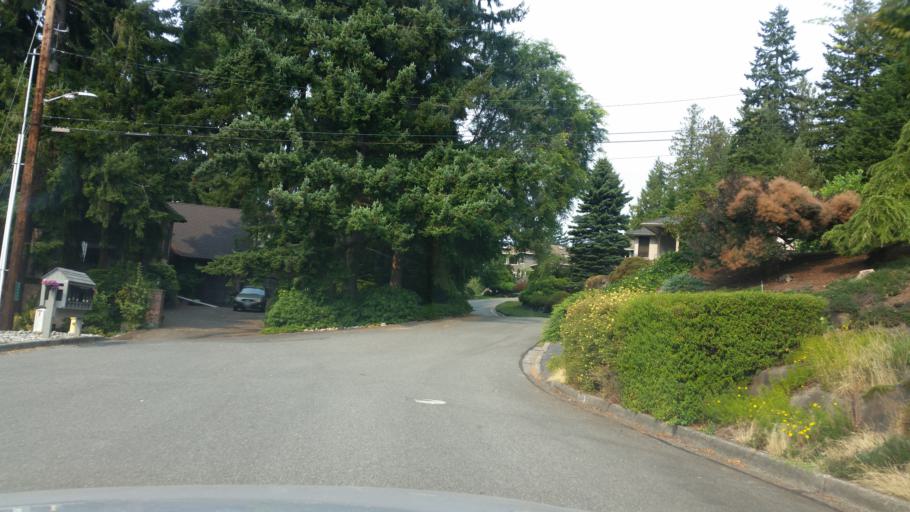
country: US
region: Washington
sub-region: Snohomish County
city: Edmonds
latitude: 47.8185
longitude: -122.3583
